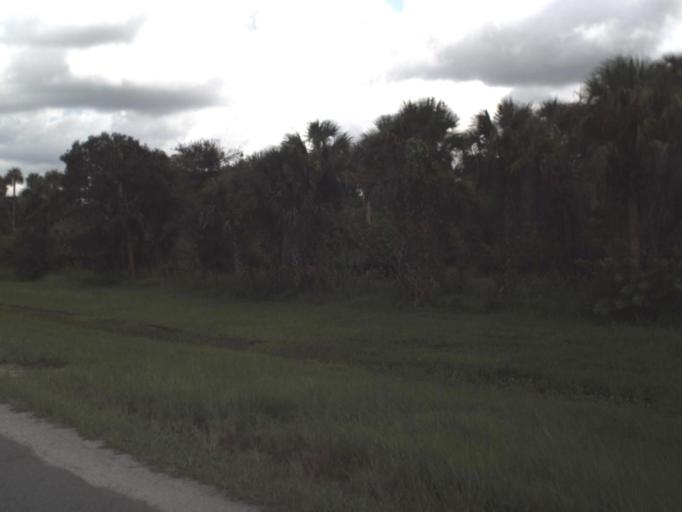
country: US
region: Florida
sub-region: Hendry County
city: LaBelle
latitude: 26.7762
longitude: -81.4374
